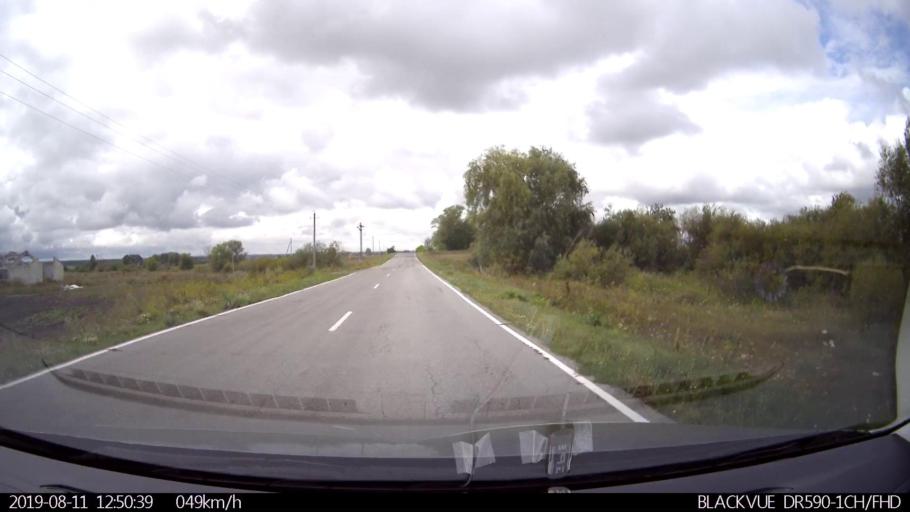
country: RU
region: Ulyanovsk
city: Ignatovka
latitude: 53.8750
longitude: 47.6701
